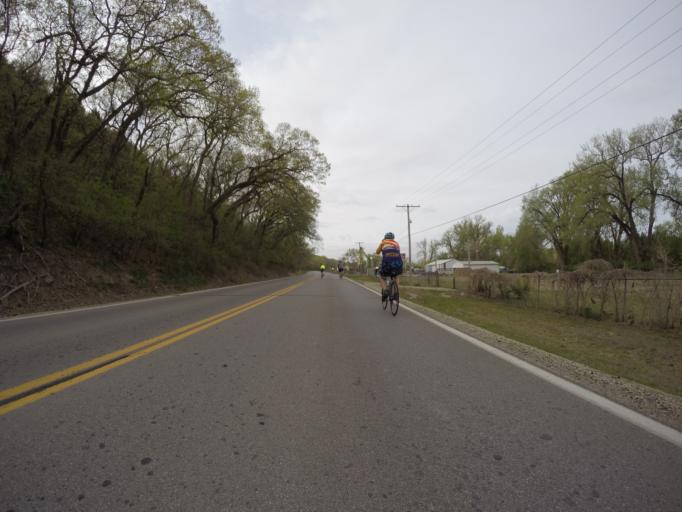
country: US
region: Kansas
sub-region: Riley County
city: Manhattan
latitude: 39.1709
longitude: -96.5532
